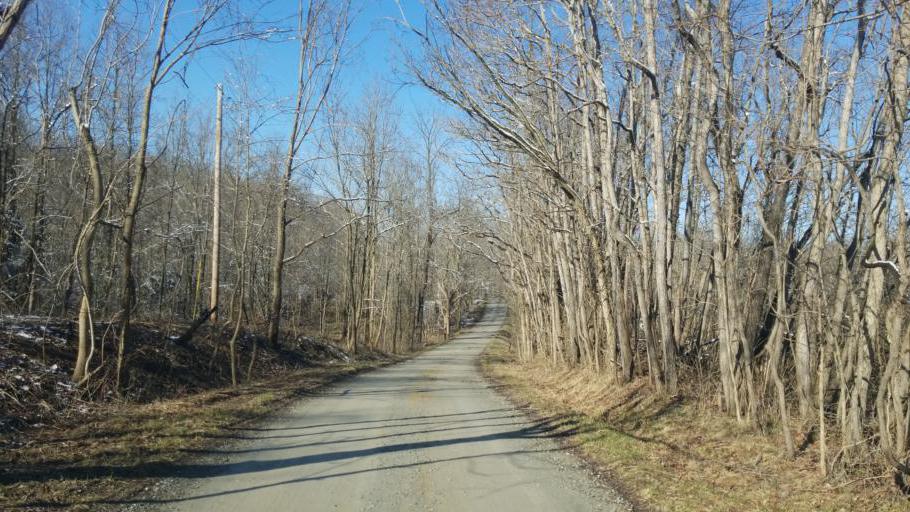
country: US
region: Ohio
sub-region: Highland County
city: Greenfield
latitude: 39.2225
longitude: -83.3607
